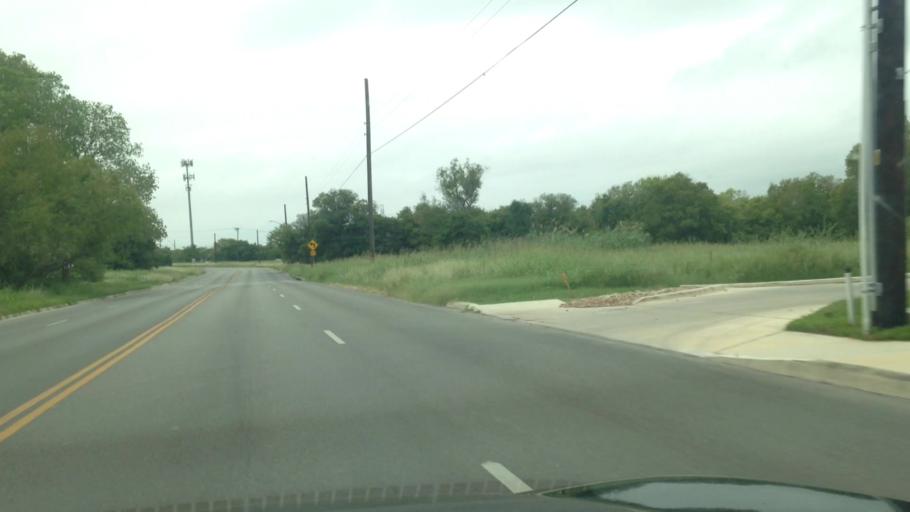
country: US
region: Texas
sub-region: Bexar County
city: Live Oak
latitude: 29.5810
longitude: -98.3993
